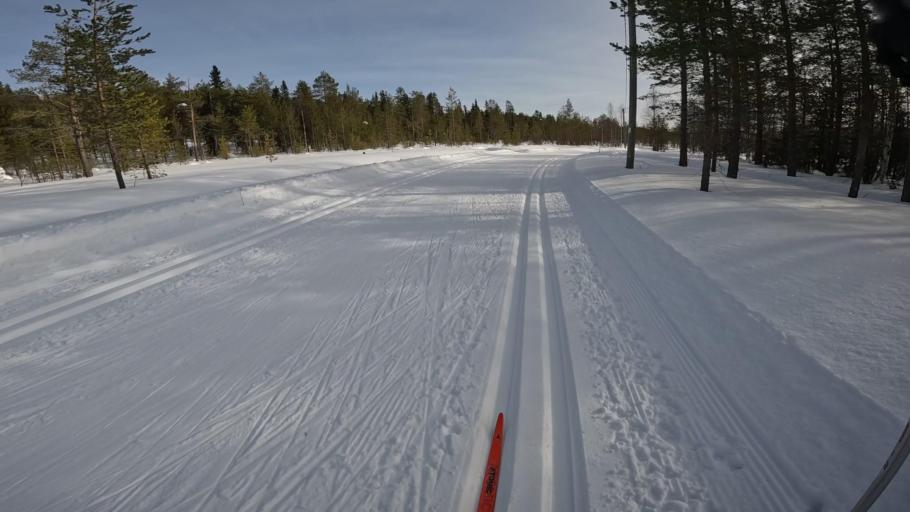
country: FI
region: Lapland
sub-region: Itae-Lappi
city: Salla
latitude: 66.7524
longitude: 28.7835
